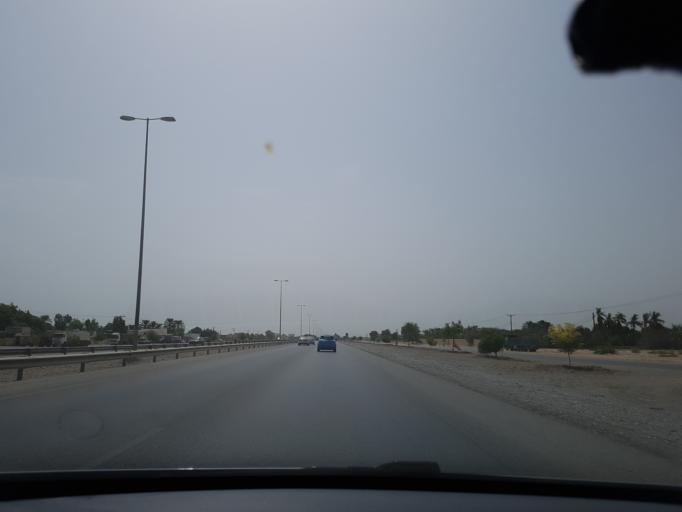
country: OM
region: Al Batinah
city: As Suwayq
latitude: 23.8135
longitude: 57.4559
